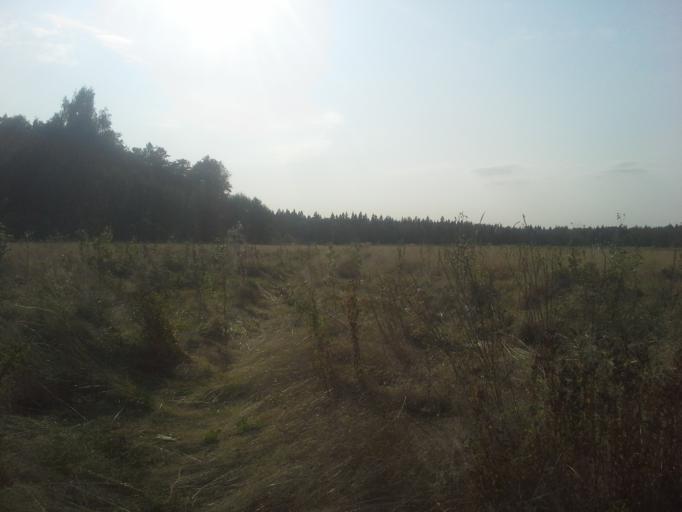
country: RU
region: Moskovskaya
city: Kievskij
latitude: 55.3819
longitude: 36.9436
